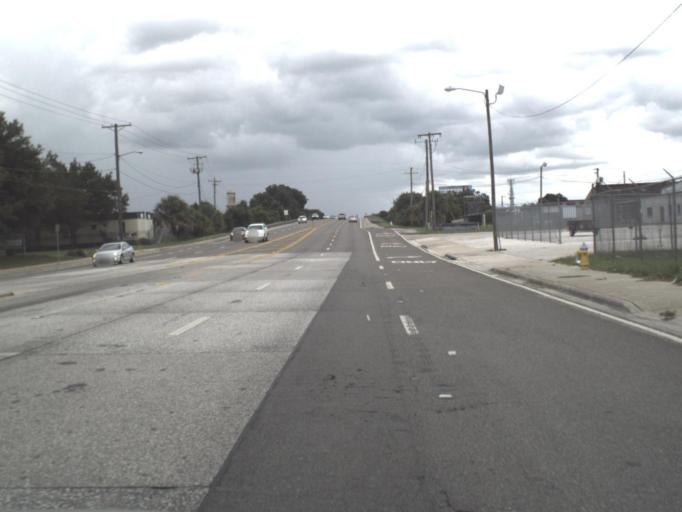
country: US
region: Florida
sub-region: Hillsborough County
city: East Lake-Orient Park
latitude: 27.9960
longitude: -82.4023
